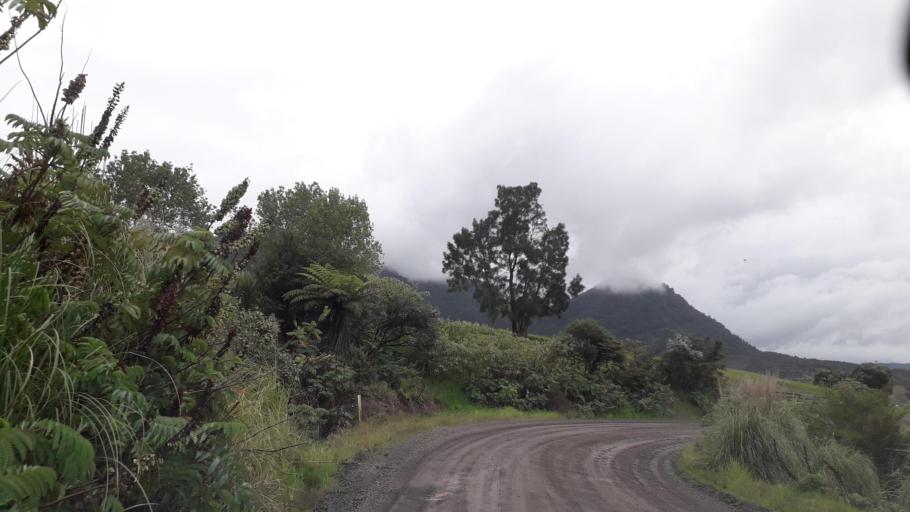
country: NZ
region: Northland
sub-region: Far North District
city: Kaitaia
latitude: -35.4114
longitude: 173.3648
